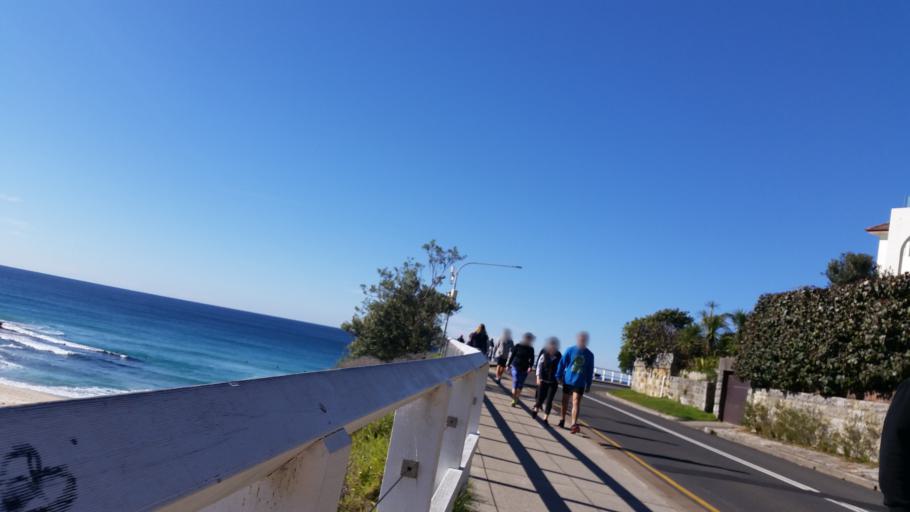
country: AU
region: New South Wales
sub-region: Waverley
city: Bronte
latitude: -33.9002
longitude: 151.2695
